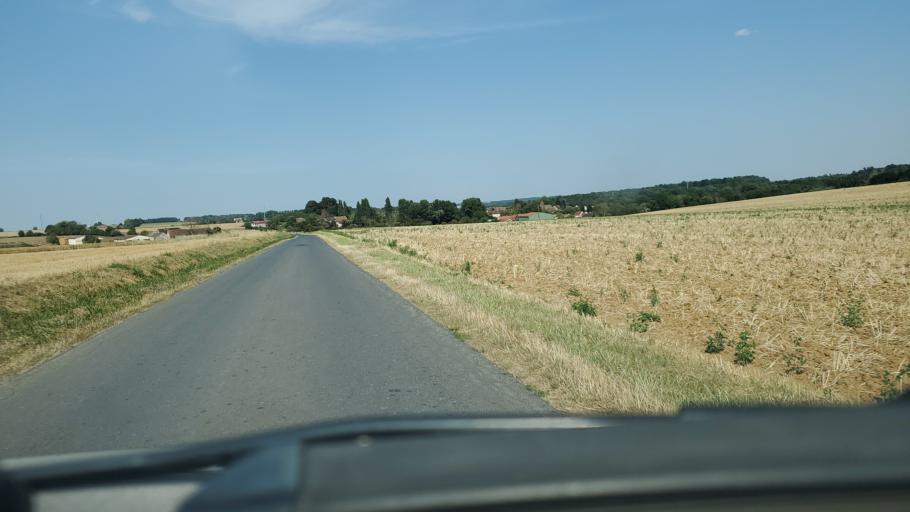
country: FR
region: Ile-de-France
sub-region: Departement de Seine-et-Marne
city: Chailly-en-Brie
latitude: 48.7707
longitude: 3.1552
